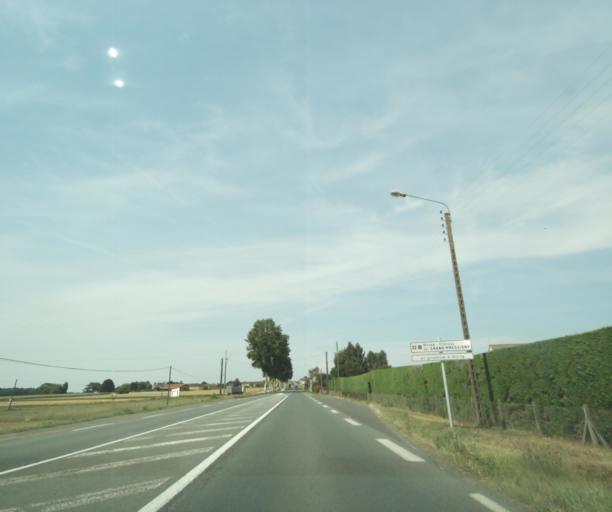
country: FR
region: Centre
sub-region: Departement d'Indre-et-Loire
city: La Celle-Saint-Avant
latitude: 47.0153
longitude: 0.6025
